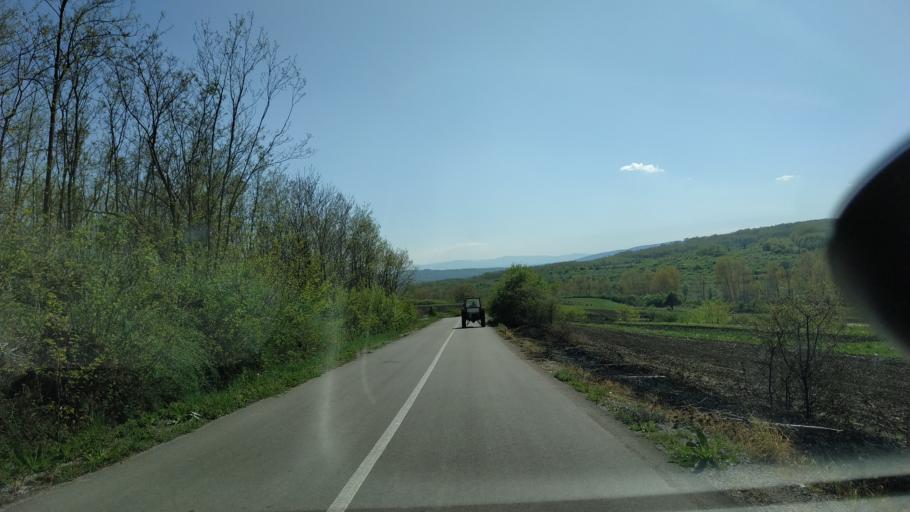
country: RS
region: Central Serbia
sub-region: Zajecarski Okrug
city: Soko Banja
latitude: 43.4896
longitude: 21.8706
